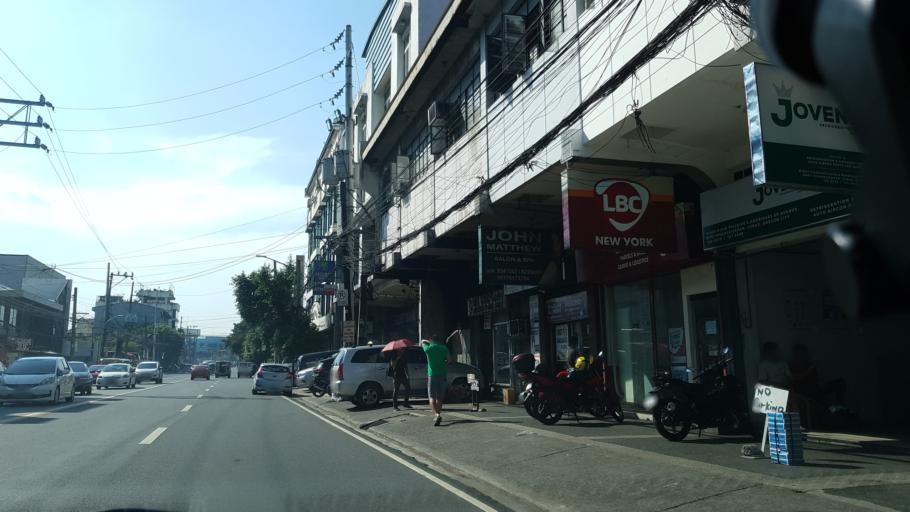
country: PH
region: Metro Manila
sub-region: San Juan
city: San Juan
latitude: 14.6232
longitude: 121.0450
